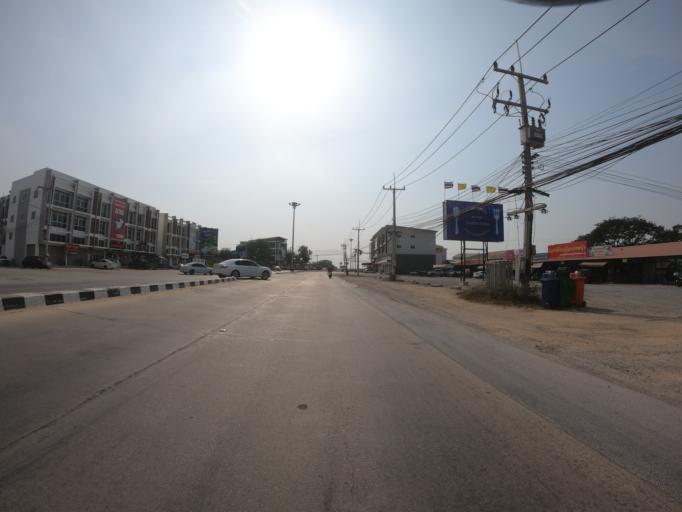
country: TH
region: Phra Nakhon Si Ayutthaya
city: Phra Nakhon Si Ayutthaya
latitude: 14.3394
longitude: 100.5985
